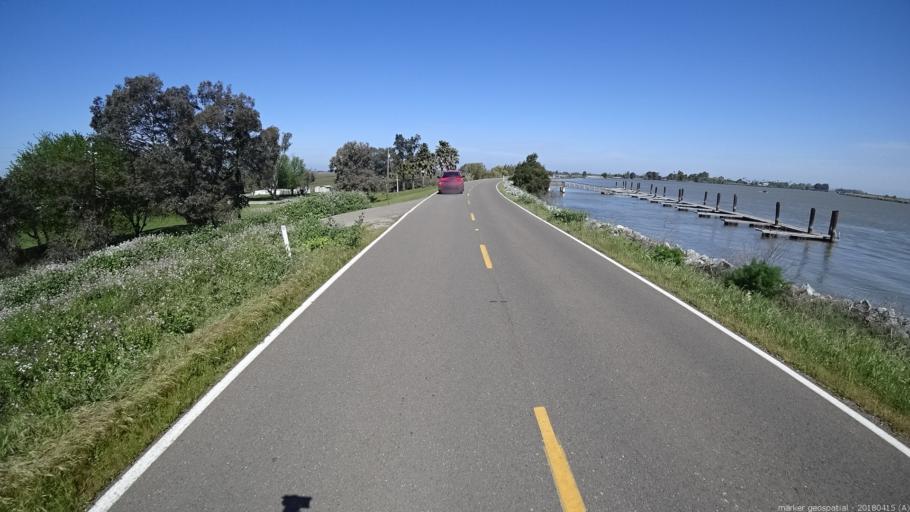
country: US
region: California
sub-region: Contra Costa County
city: Bethel Island
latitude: 38.1132
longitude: -121.5856
